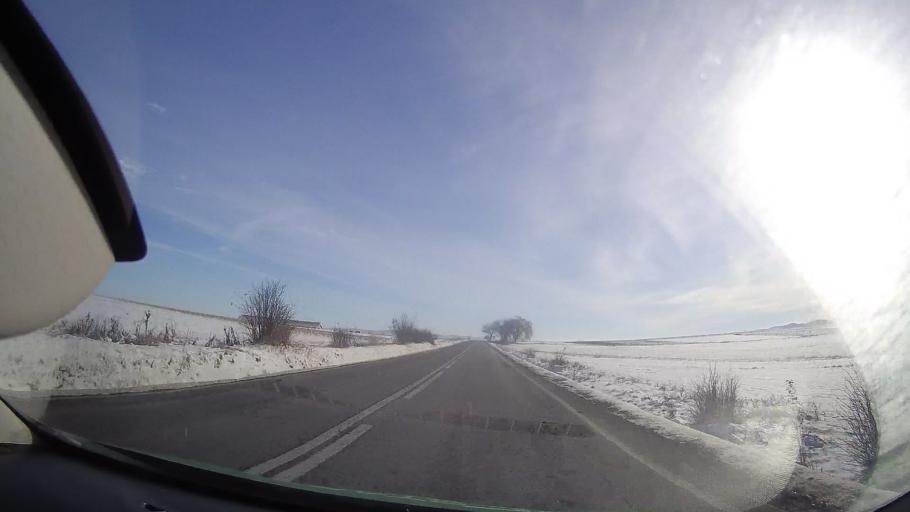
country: RO
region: Neamt
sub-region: Comuna Baltatesti
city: Valea Seaca
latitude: 47.1583
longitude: 26.3207
